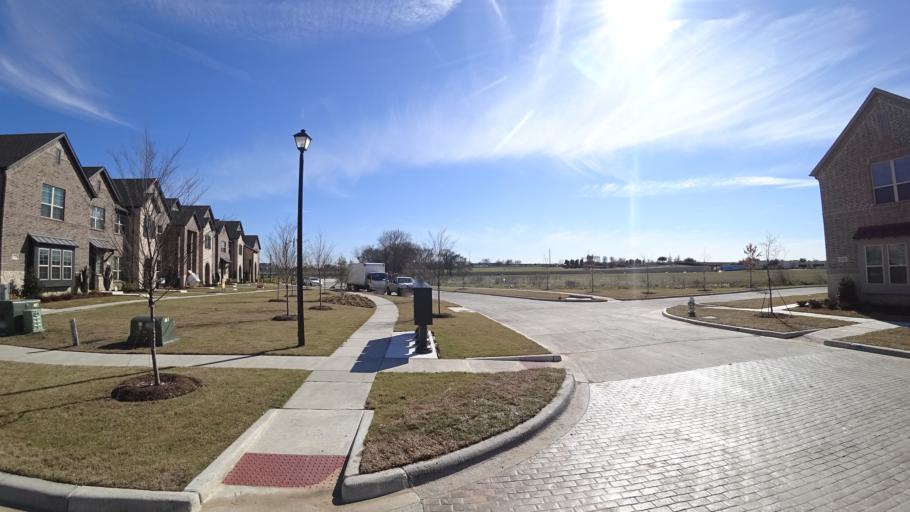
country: US
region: Texas
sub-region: Denton County
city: Lewisville
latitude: 32.9955
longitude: -96.9715
